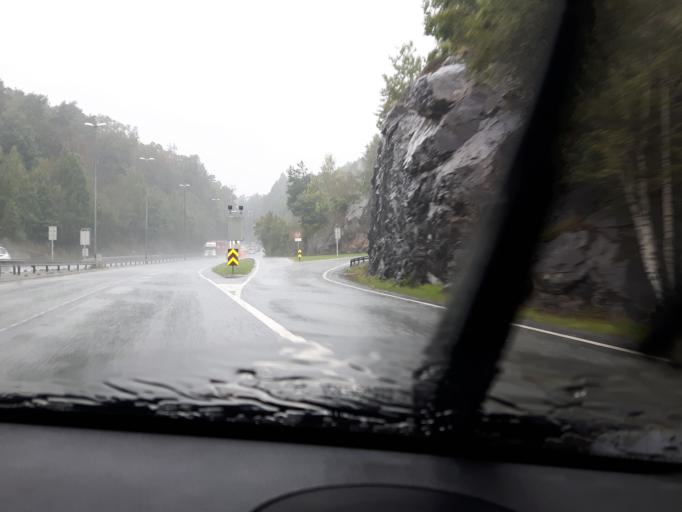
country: NO
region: Vest-Agder
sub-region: Kristiansand
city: Strai
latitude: 58.1414
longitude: 7.9388
